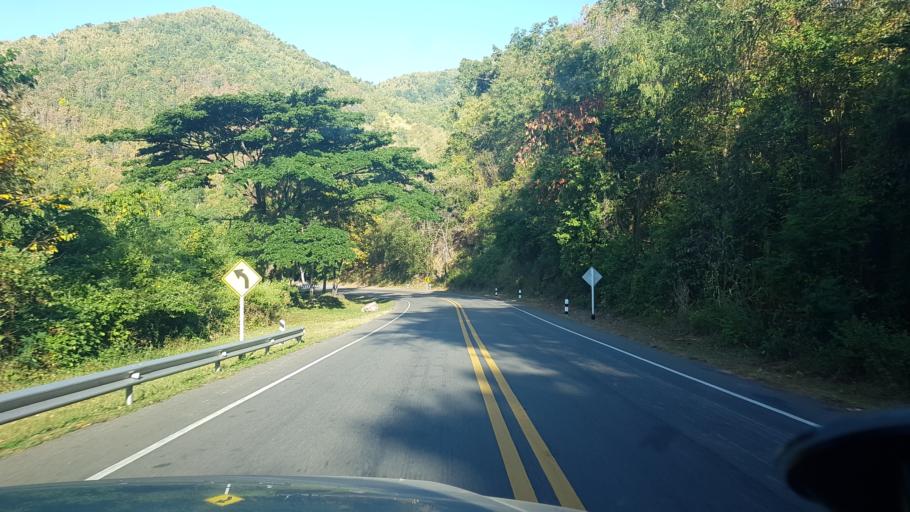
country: TH
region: Phetchabun
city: Lom Sak
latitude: 16.7468
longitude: 101.3980
